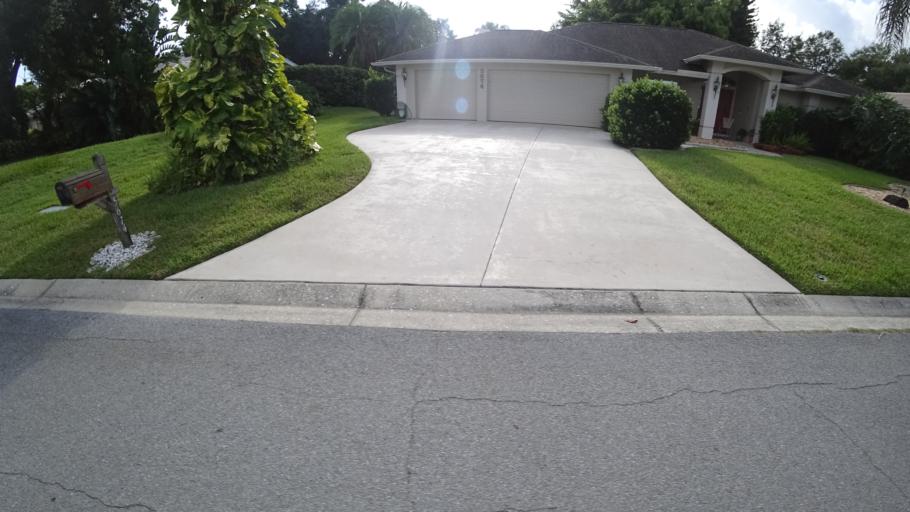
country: US
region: Florida
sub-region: Sarasota County
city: Desoto Lakes
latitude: 27.4205
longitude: -82.4896
